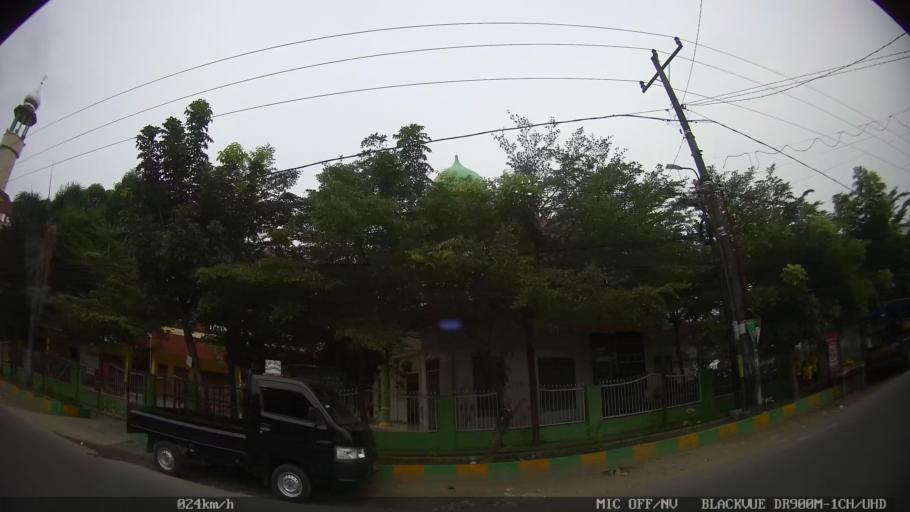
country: ID
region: North Sumatra
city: Medan
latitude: 3.5761
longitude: 98.7267
